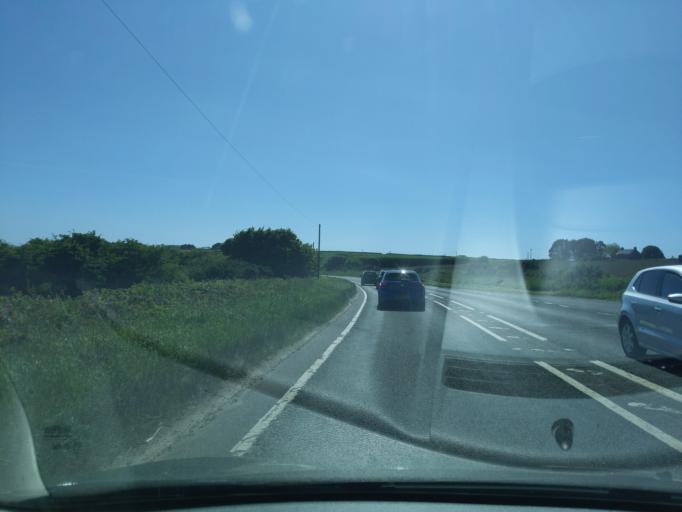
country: GB
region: England
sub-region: Cornwall
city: Wendron
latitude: 50.1493
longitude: -5.2085
